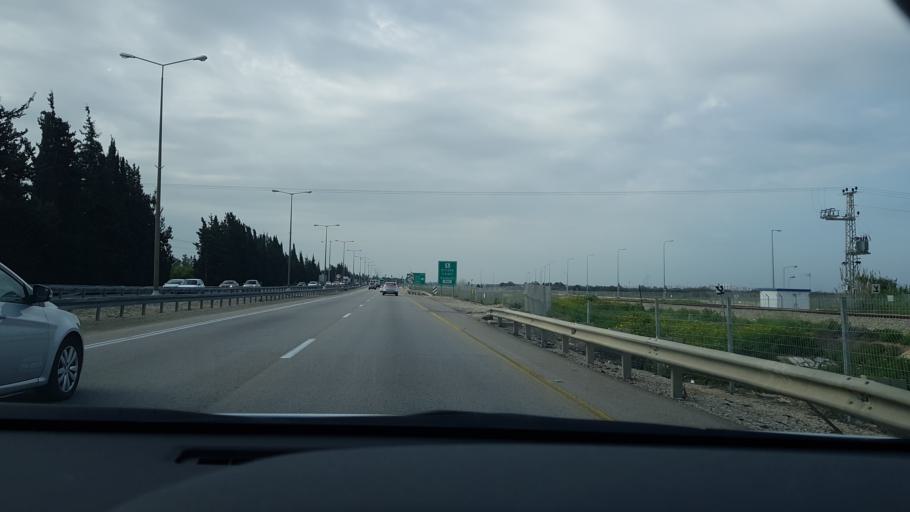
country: IL
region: Southern District
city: Ashdod
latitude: 31.7301
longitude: 34.6389
